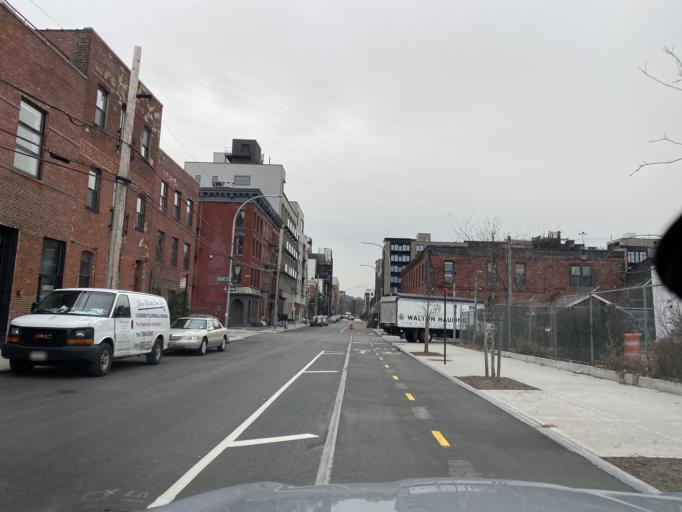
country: US
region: New York
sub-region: Queens County
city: Long Island City
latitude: 40.7337
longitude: -73.9600
